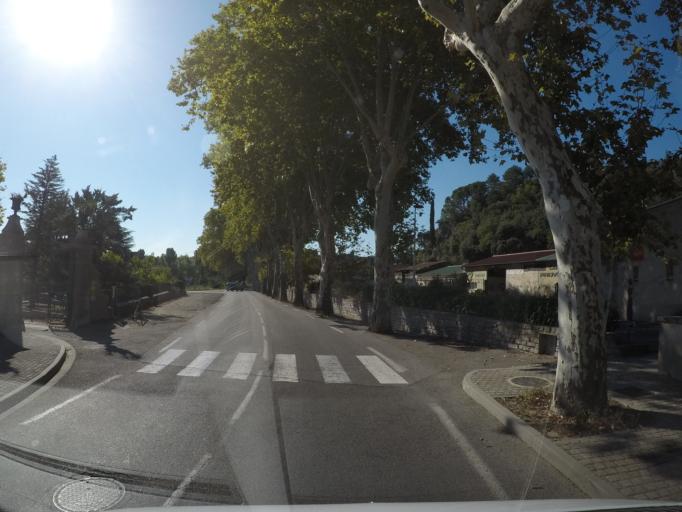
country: FR
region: Languedoc-Roussillon
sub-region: Departement du Gard
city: Anduze
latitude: 44.0497
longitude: 3.9852
